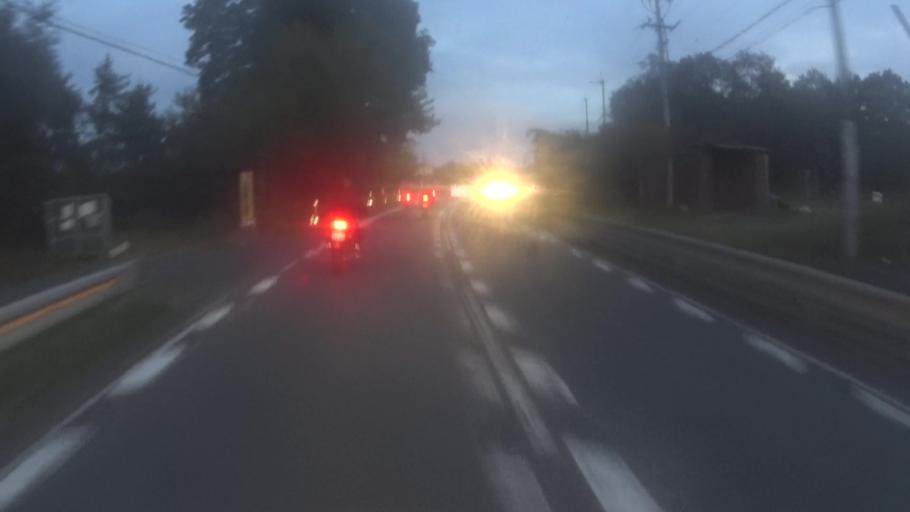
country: JP
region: Kyoto
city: Ayabe
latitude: 35.1736
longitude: 135.4243
